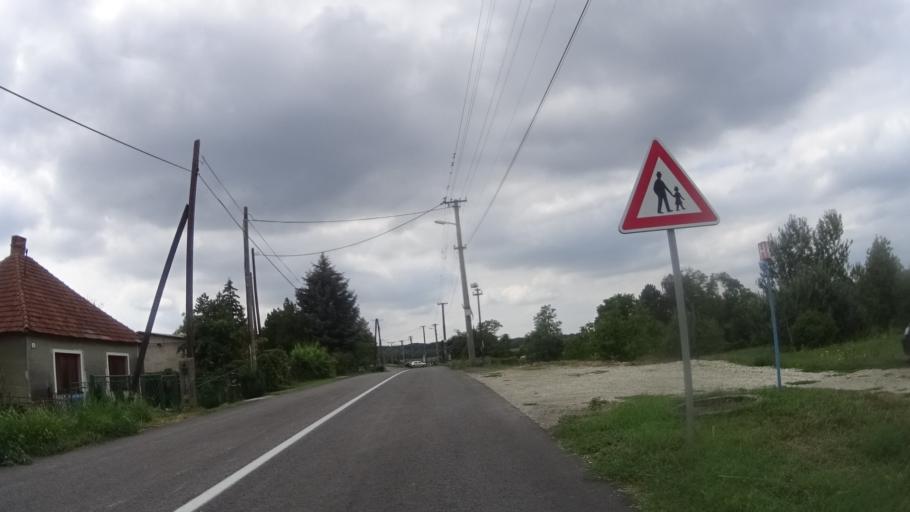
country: SK
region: Trnavsky
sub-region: Okres Dunajska Streda
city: Velky Meder
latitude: 47.7529
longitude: 17.8105
